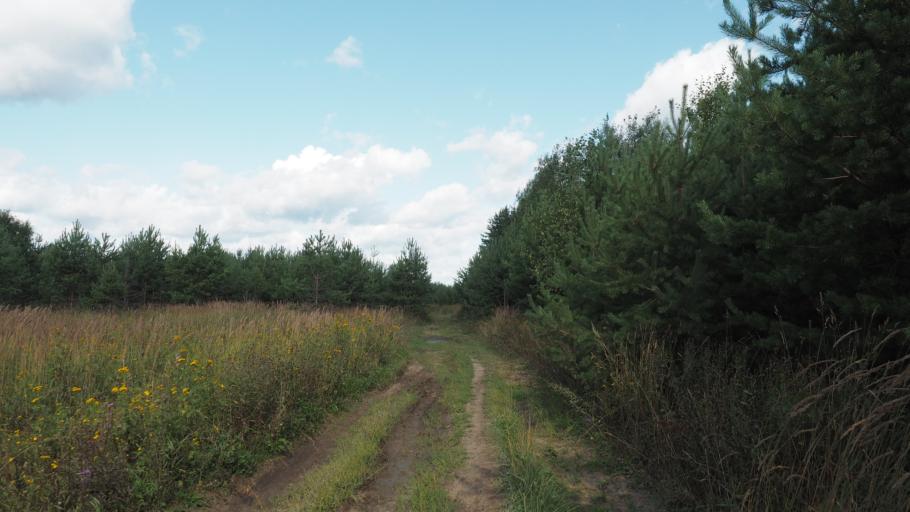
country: RU
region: Moskovskaya
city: Ramenskoye
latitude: 55.5950
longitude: 38.2878
